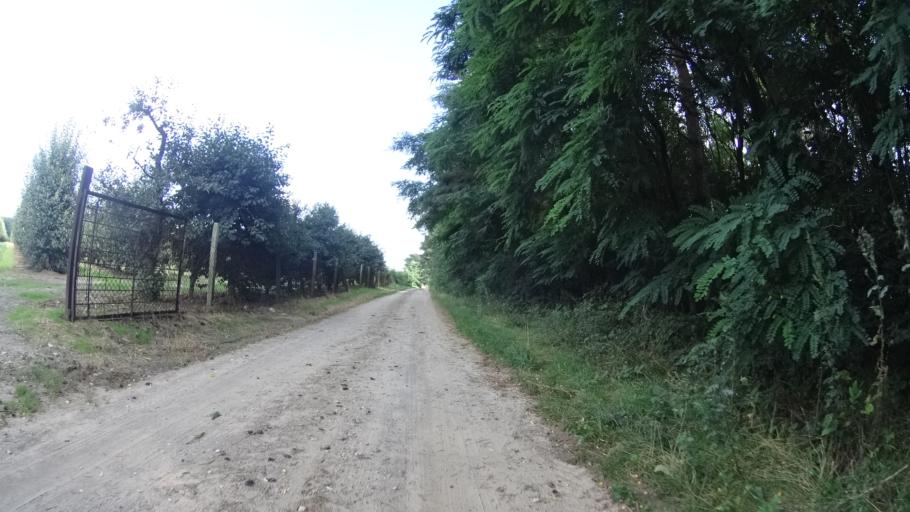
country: PL
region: Masovian Voivodeship
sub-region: Powiat grojecki
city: Mogielnica
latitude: 51.6781
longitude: 20.7659
